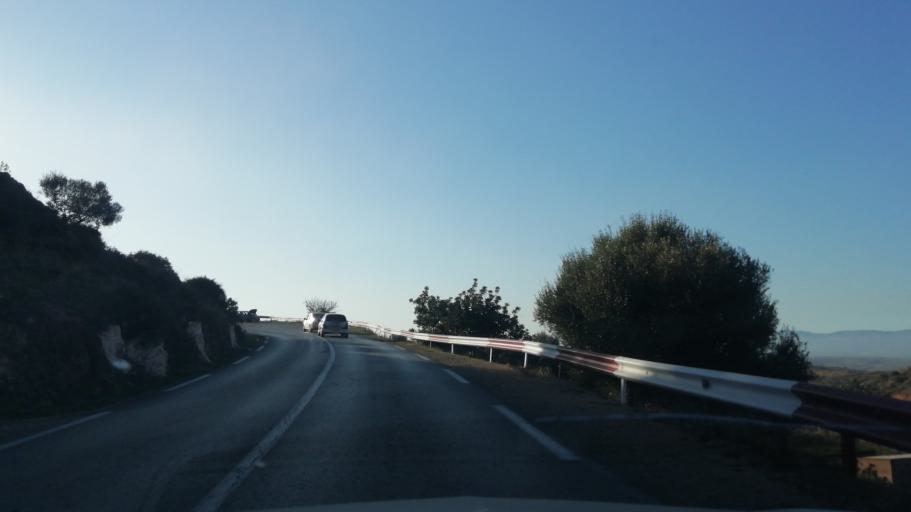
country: DZ
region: Tlemcen
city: Beni Mester
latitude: 34.8564
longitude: -1.4479
